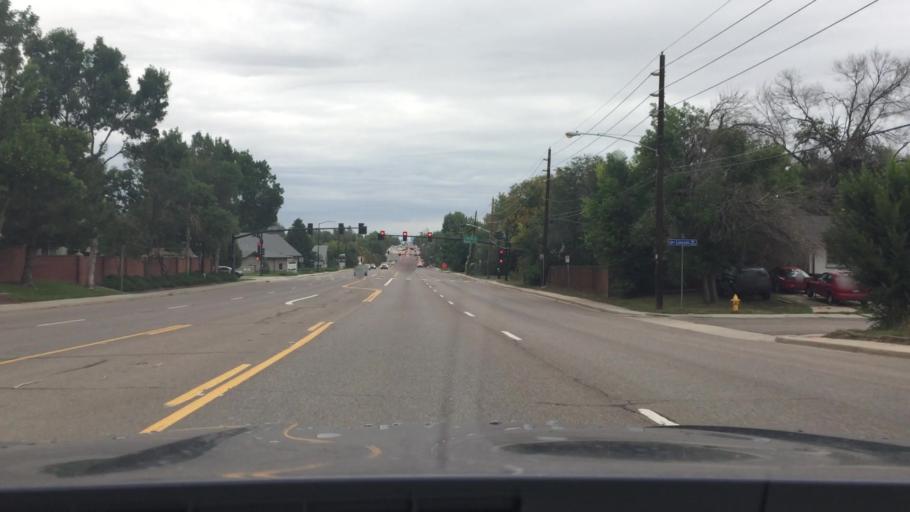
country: US
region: Colorado
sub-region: Arapahoe County
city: Southglenn
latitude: 39.5875
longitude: -104.9884
